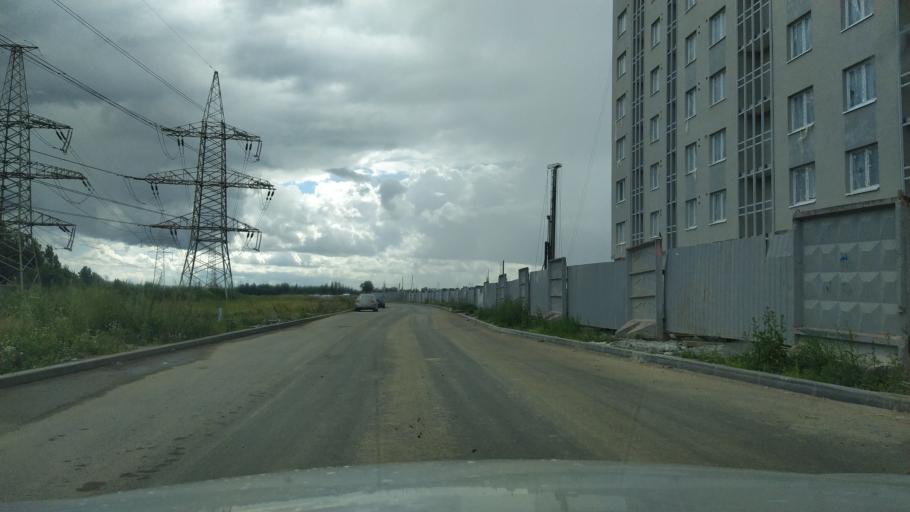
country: RU
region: St.-Petersburg
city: Krasnogvargeisky
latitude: 60.0030
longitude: 30.4831
